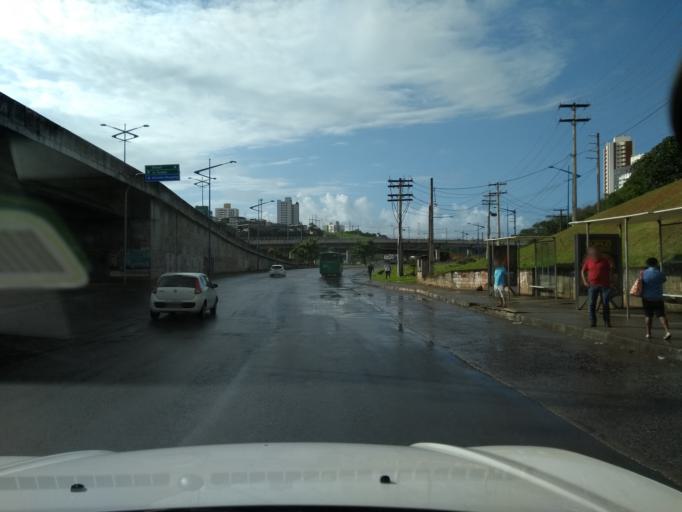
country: BR
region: Bahia
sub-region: Salvador
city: Salvador
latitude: -12.9702
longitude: -38.4792
